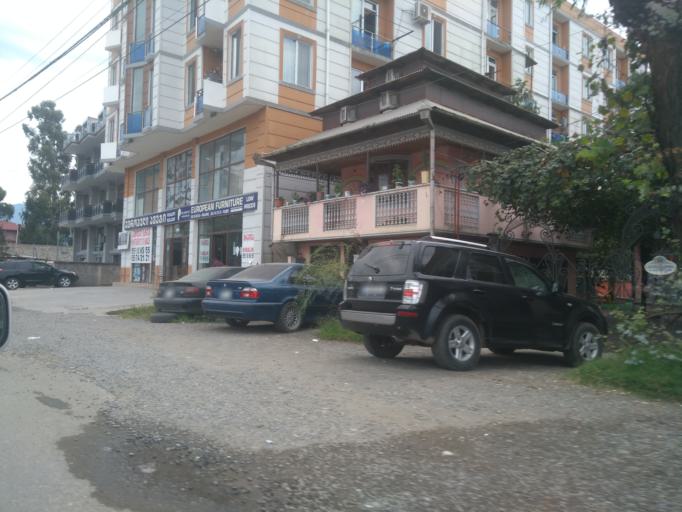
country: GE
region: Ajaria
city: Batumi
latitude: 41.6163
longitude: 41.6199
